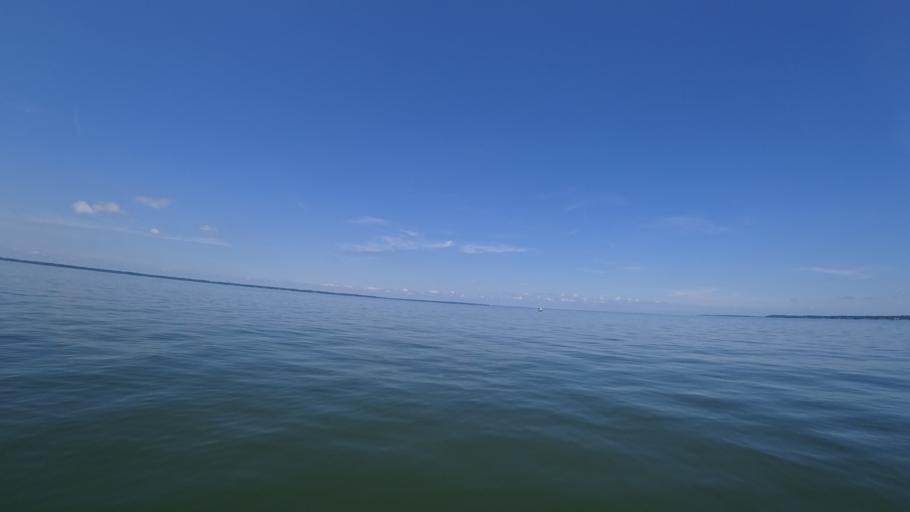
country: US
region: Virginia
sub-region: City of Newport News
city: Newport News
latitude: 37.0058
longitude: -76.4748
